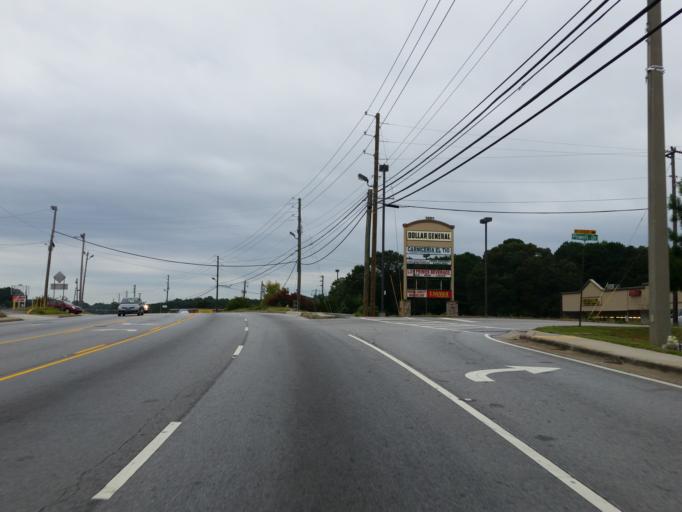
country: US
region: Georgia
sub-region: Cobb County
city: Mableton
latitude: 33.8152
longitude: -84.5958
